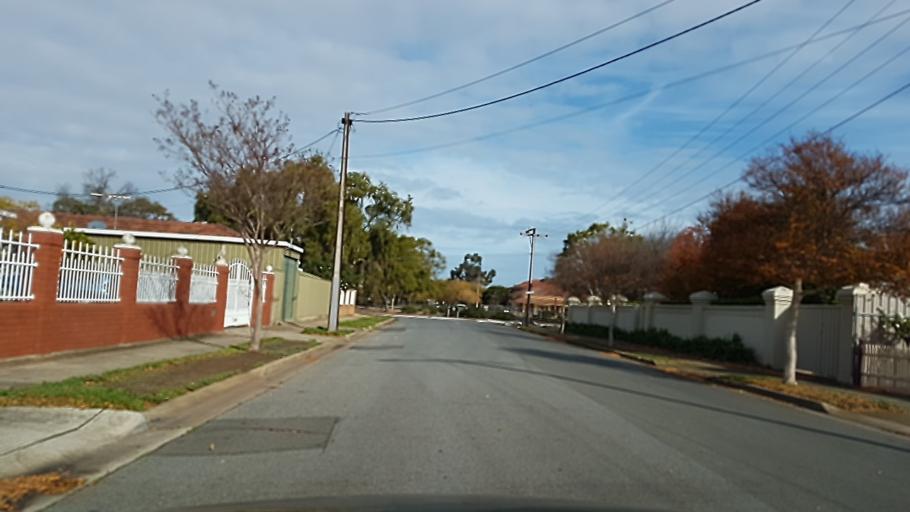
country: AU
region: South Australia
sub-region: Charles Sturt
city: Woodville North
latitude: -34.8791
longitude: 138.5417
